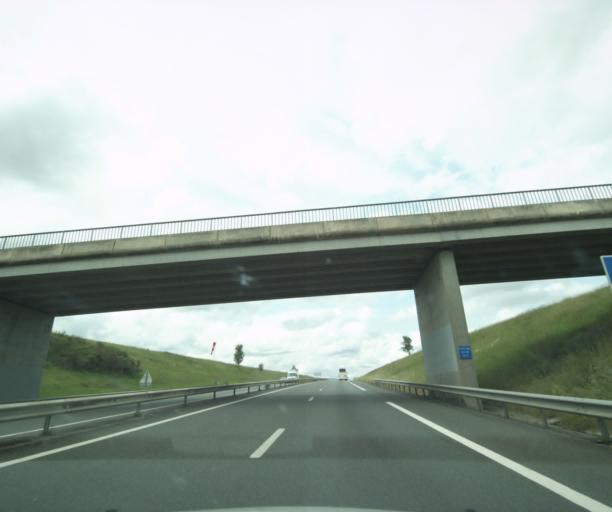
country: FR
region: Auvergne
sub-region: Departement de l'Allier
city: Ebreuil
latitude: 46.1284
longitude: 3.1155
